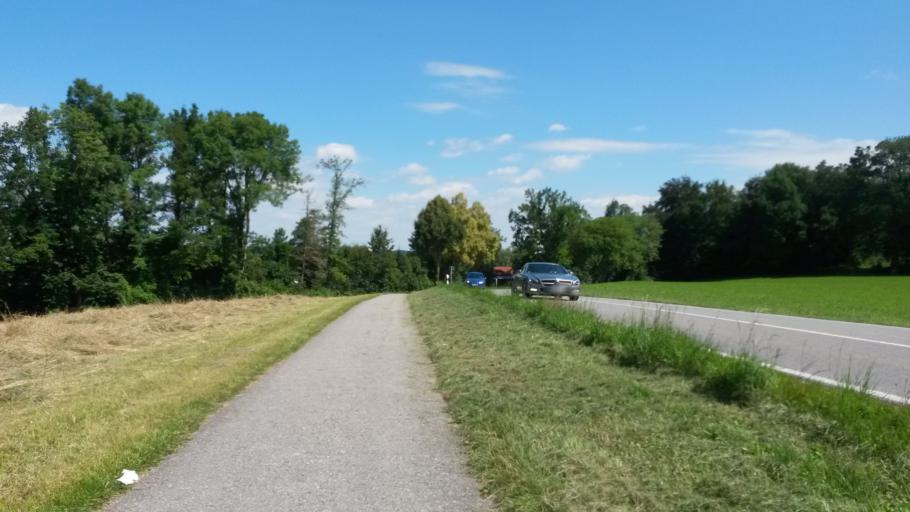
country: DE
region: Bavaria
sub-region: Upper Bavaria
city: Chieming
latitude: 47.8750
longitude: 12.5286
